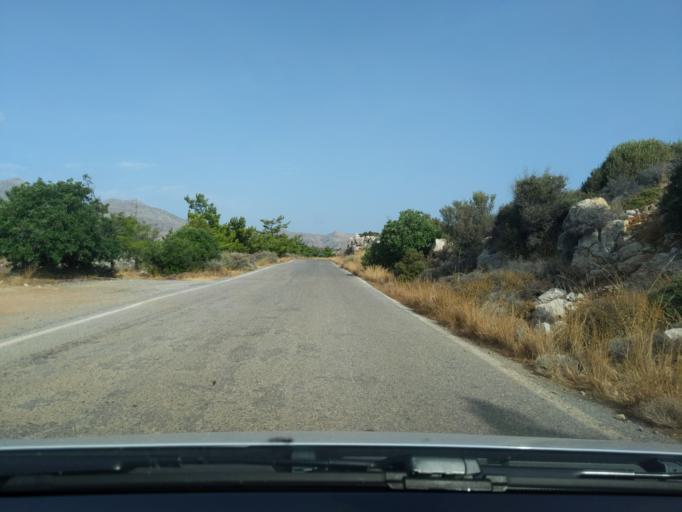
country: GR
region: Crete
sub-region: Nomos Lasithiou
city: Palekastro
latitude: 35.0859
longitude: 26.2439
